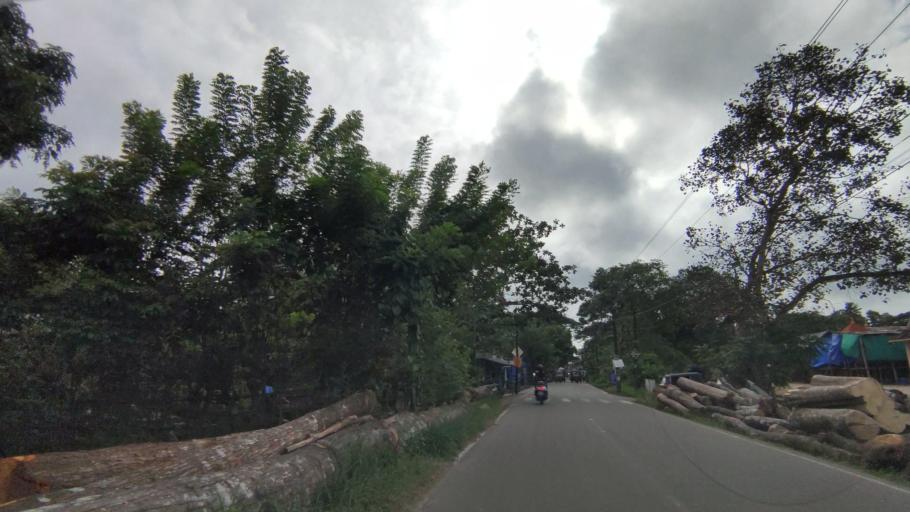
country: IN
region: Kerala
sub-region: Alappuzha
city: Shertallai
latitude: 9.6415
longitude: 76.3554
